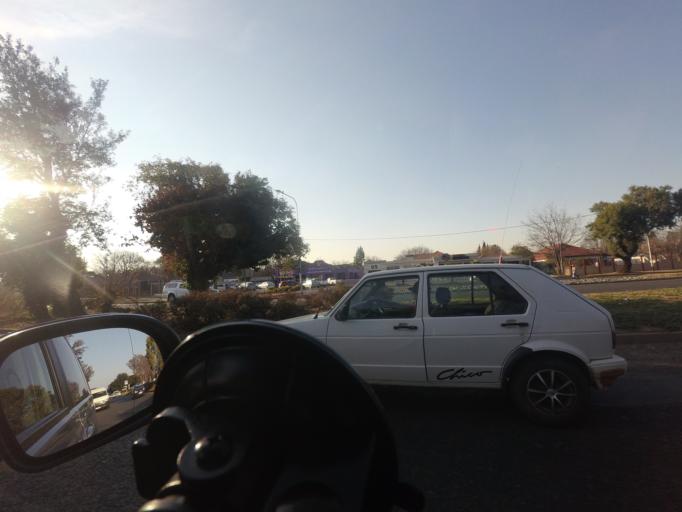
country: ZA
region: Gauteng
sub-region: Sedibeng District Municipality
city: Vereeniging
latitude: -26.6577
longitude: 27.9644
